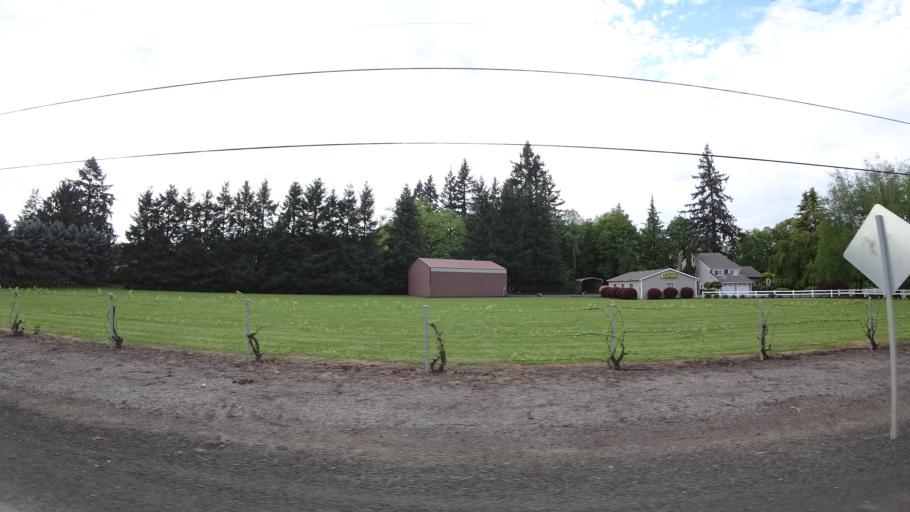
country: US
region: Oregon
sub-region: Washington County
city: Hillsboro
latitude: 45.4813
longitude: -122.9846
